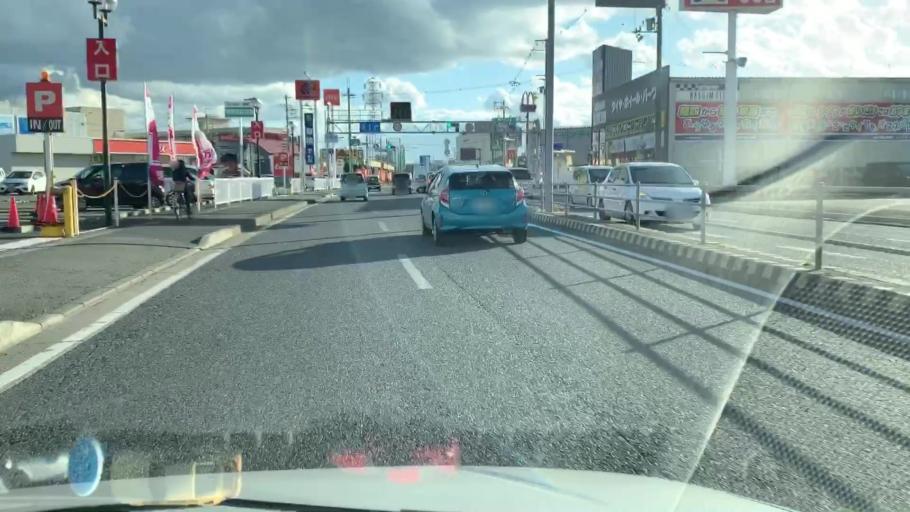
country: JP
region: Wakayama
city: Wakayama-shi
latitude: 34.2429
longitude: 135.1518
